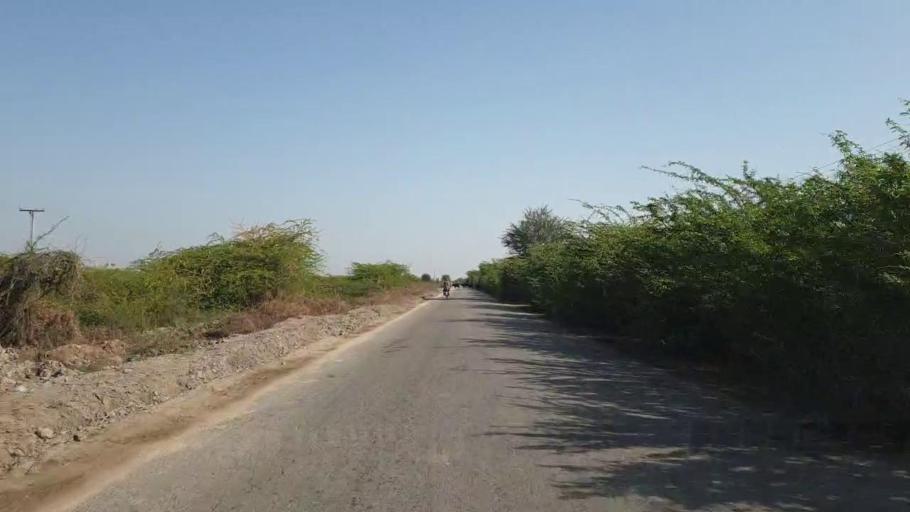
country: PK
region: Sindh
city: Chor
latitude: 25.4724
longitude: 69.7715
